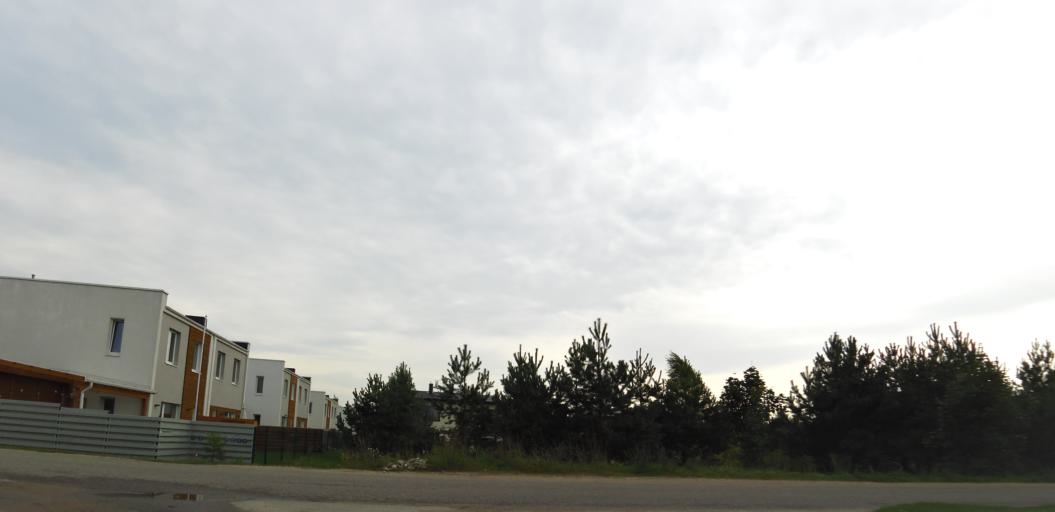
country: LT
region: Vilnius County
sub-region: Vilnius
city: Fabijoniskes
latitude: 54.7533
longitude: 25.2352
